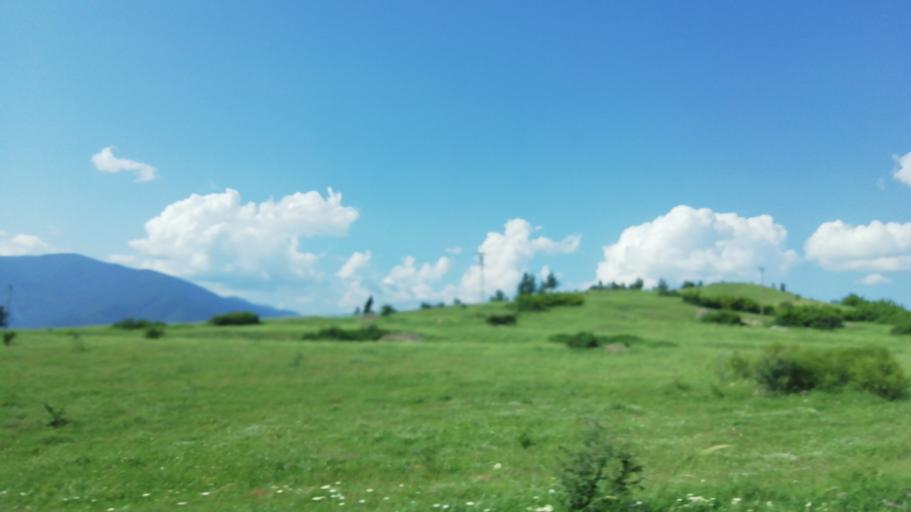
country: TR
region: Karabuk
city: Karabuk
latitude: 41.1309
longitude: 32.5726
